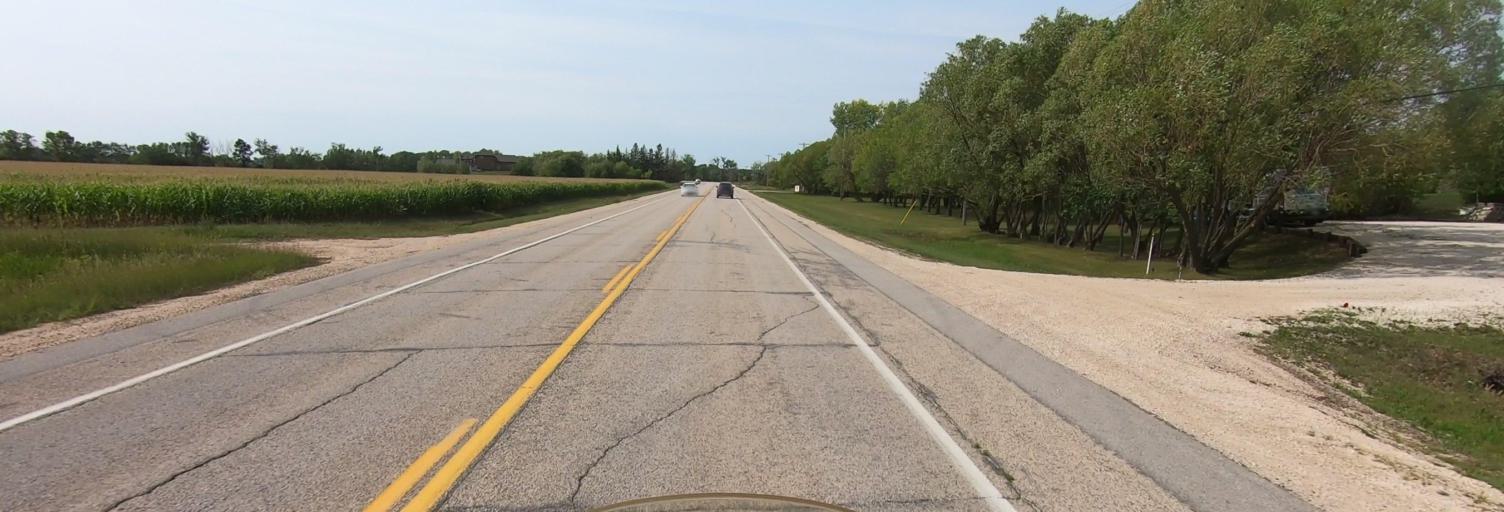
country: CA
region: Manitoba
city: Niverville
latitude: 49.6926
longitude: -97.1043
